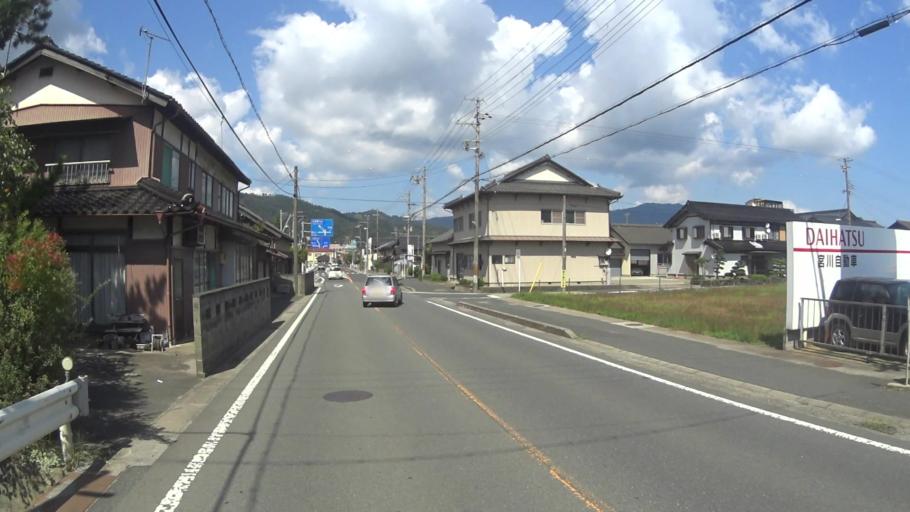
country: JP
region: Kyoto
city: Miyazu
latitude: 35.5610
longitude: 135.1534
